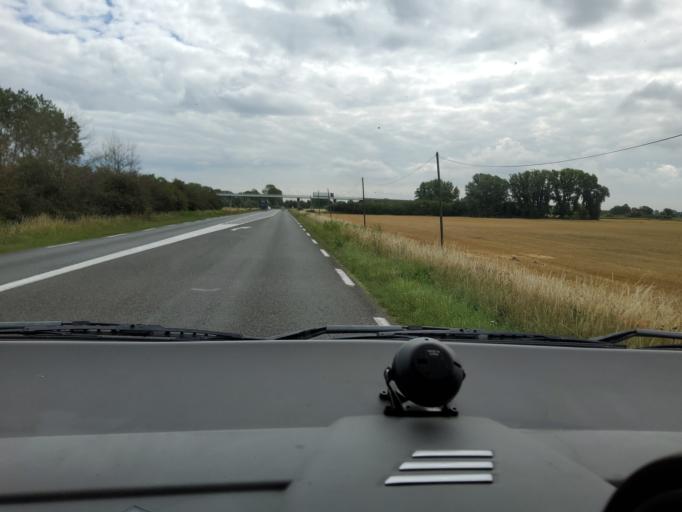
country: FR
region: Nord-Pas-de-Calais
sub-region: Departement du Nord
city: Loon-Plage
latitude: 50.9957
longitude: 2.1918
